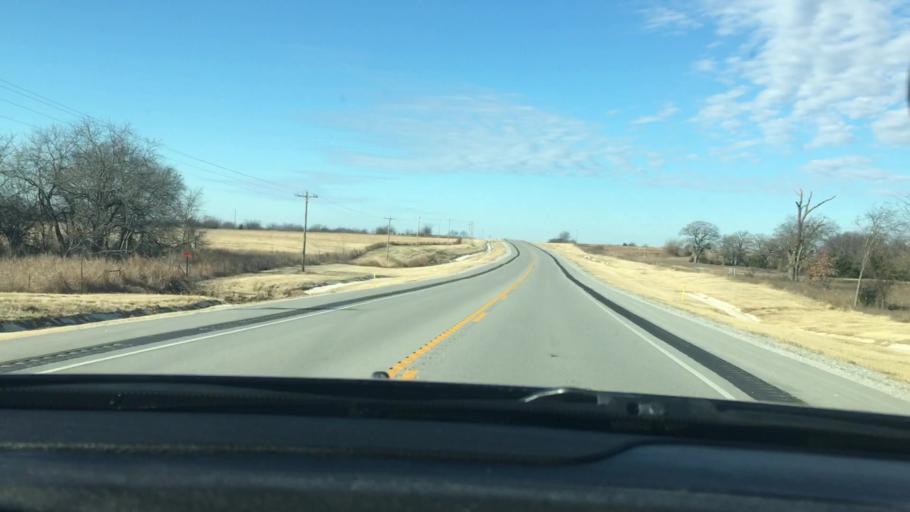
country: US
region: Oklahoma
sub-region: Love County
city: Marietta
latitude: 33.9405
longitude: -97.2236
